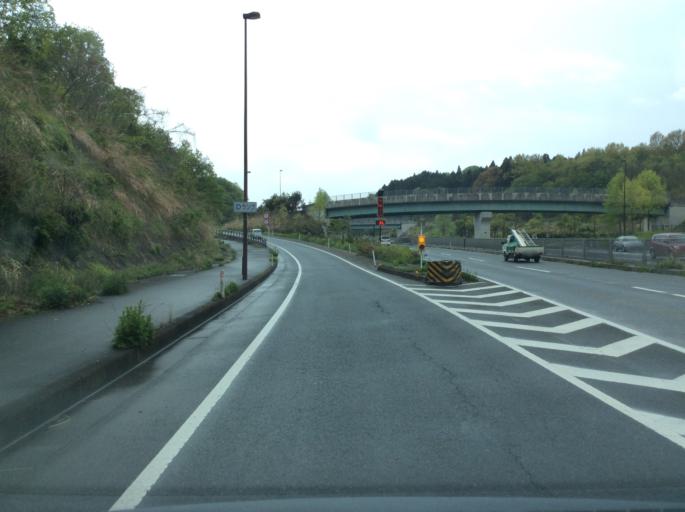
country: JP
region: Fukushima
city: Iwaki
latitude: 37.0216
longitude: 140.8941
